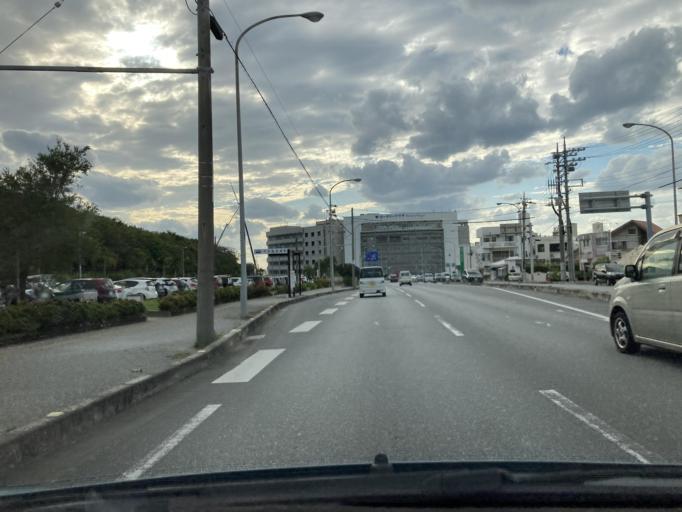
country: JP
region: Okinawa
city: Okinawa
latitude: 26.3637
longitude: 127.7591
